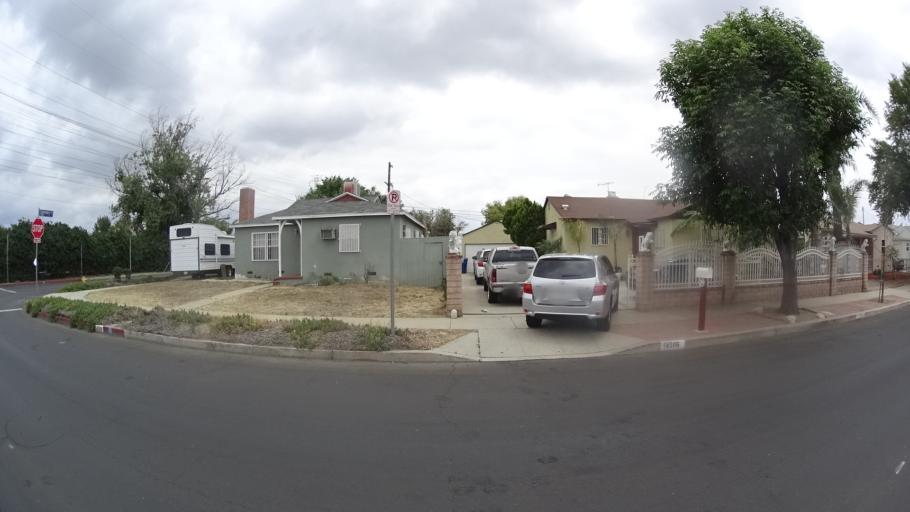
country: US
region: California
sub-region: Los Angeles County
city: San Fernando
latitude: 34.2520
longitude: -118.4485
